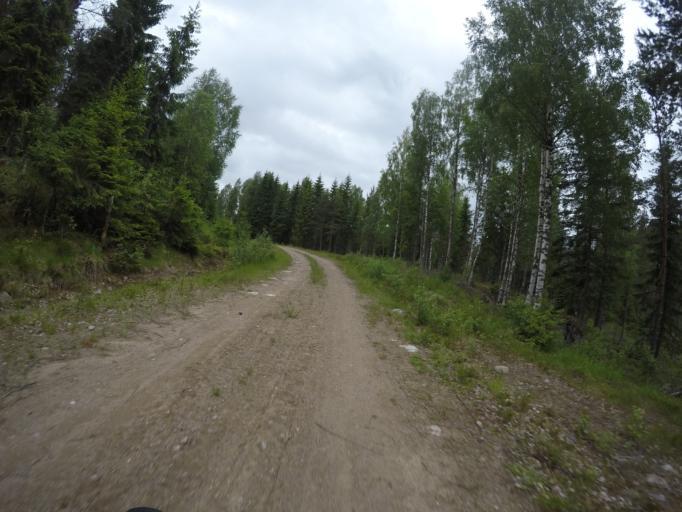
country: SE
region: Dalarna
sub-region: Ludvika Kommun
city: Abborrberget
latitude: 60.0658
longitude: 14.5606
